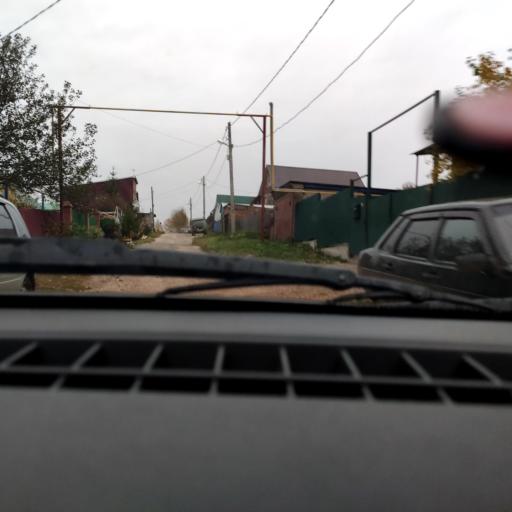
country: RU
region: Bashkortostan
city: Ufa
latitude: 54.8337
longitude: 56.1444
